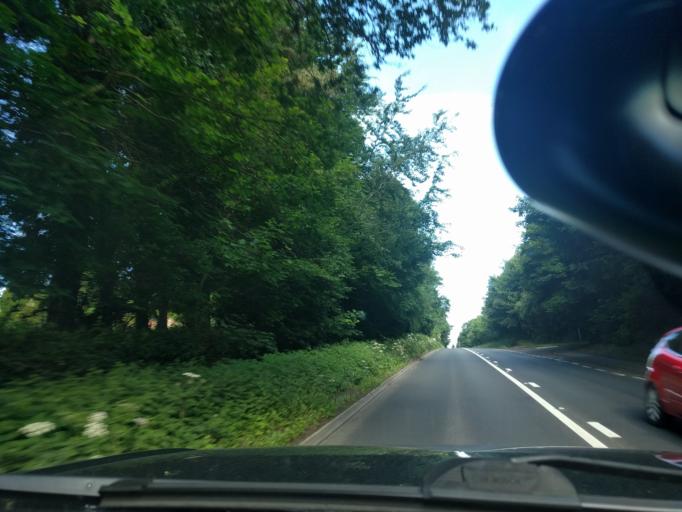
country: GB
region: England
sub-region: Wiltshire
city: Bremhill
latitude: 51.4375
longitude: -2.0335
